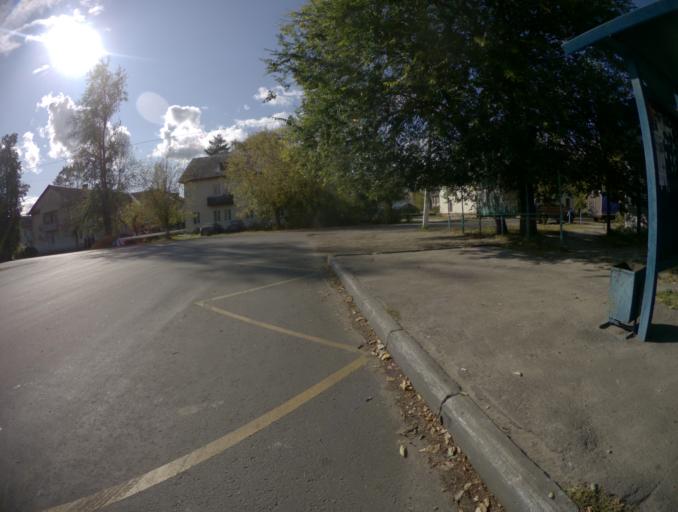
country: RU
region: Moskovskaya
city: Kerva
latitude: 55.6106
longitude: 39.5787
